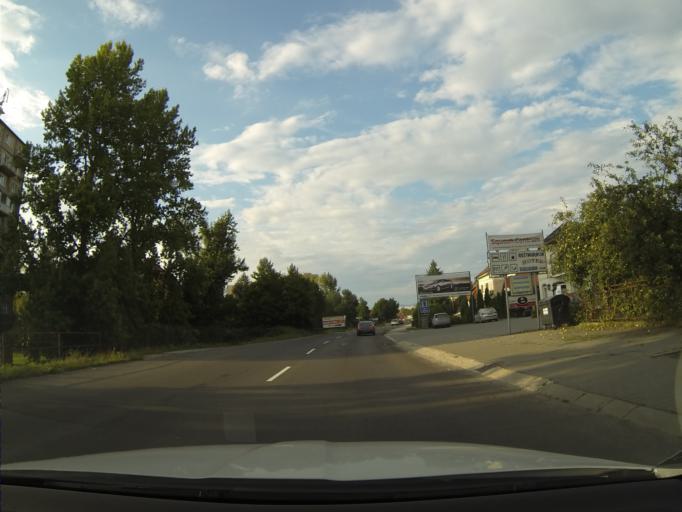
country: SK
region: Nitriansky
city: Prievidza
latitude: 48.7768
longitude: 18.6261
